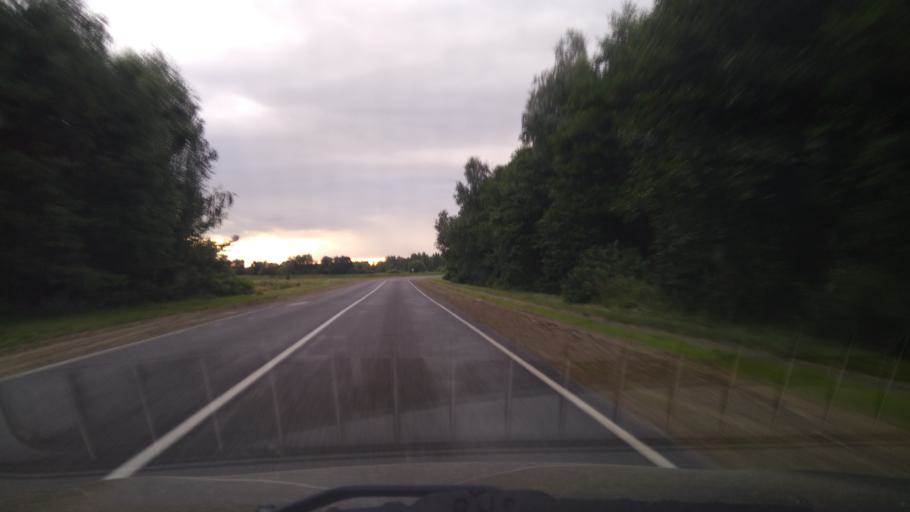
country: BY
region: Brest
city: Byaroza
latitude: 52.4161
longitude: 24.9833
